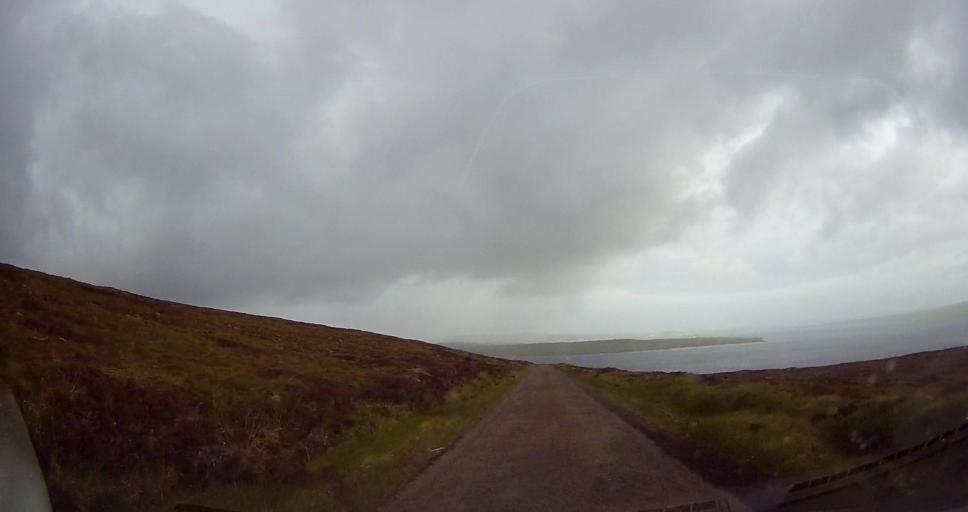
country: GB
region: Scotland
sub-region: Orkney Islands
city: Stromness
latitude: 58.8970
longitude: -3.2733
